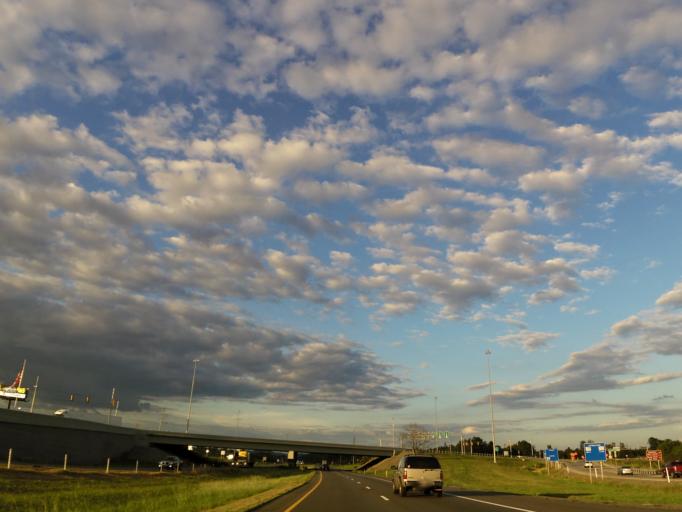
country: US
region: Tennessee
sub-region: Bradley County
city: Cleveland
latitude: 35.1511
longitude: -84.9492
